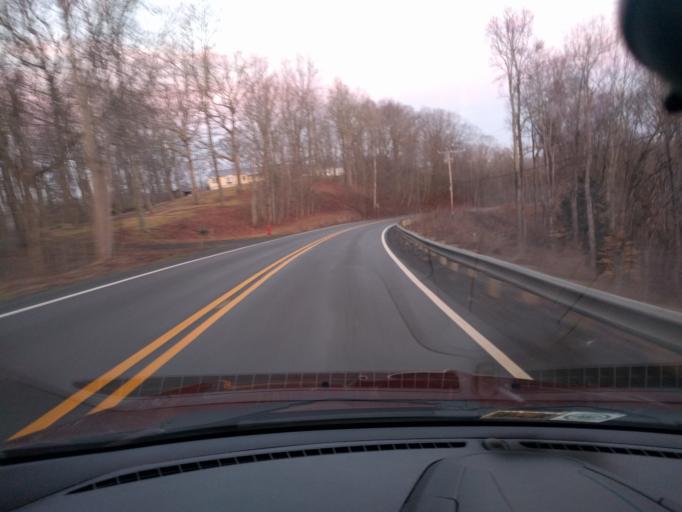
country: US
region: West Virginia
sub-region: Greenbrier County
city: Rainelle
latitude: 38.0161
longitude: -80.9067
